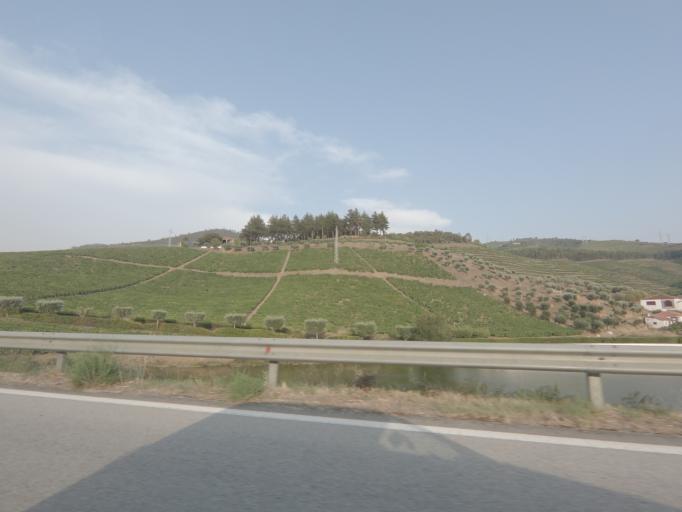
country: PT
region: Viseu
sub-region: Armamar
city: Armamar
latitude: 41.1463
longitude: -7.6872
